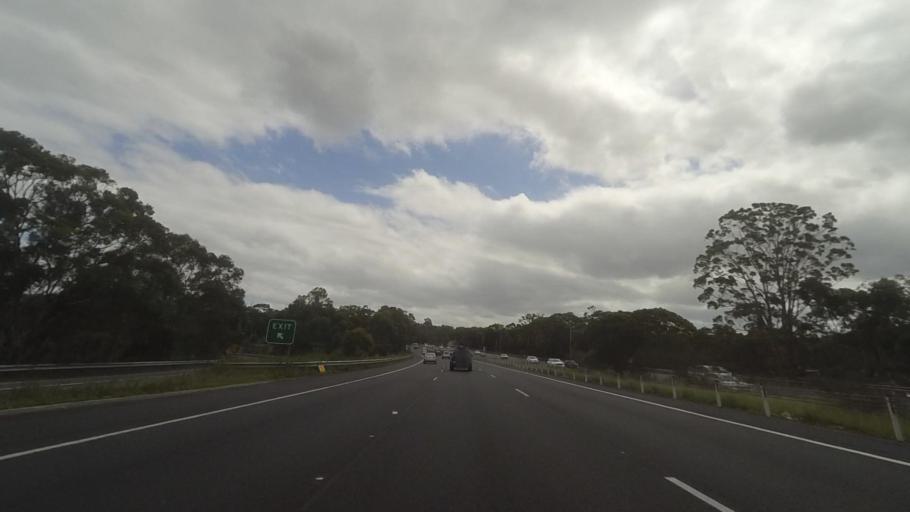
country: AU
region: New South Wales
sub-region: Gosford Shire
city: Point Clare
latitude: -33.4606
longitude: 151.1986
